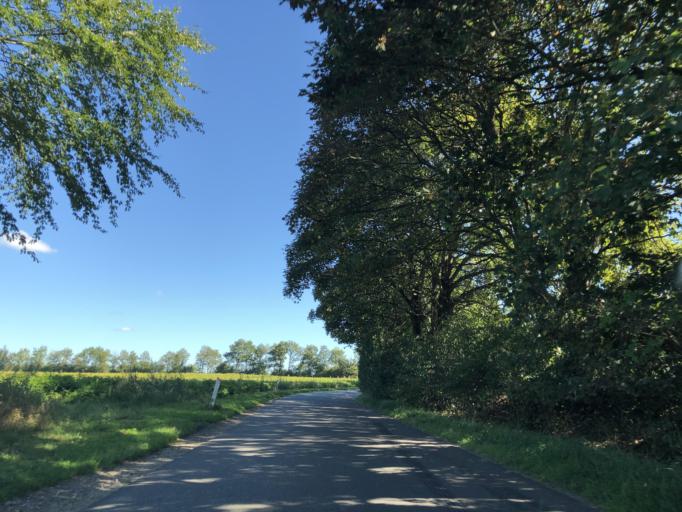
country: DK
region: Central Jutland
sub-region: Viborg Kommune
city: Karup
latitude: 56.3489
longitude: 9.1389
